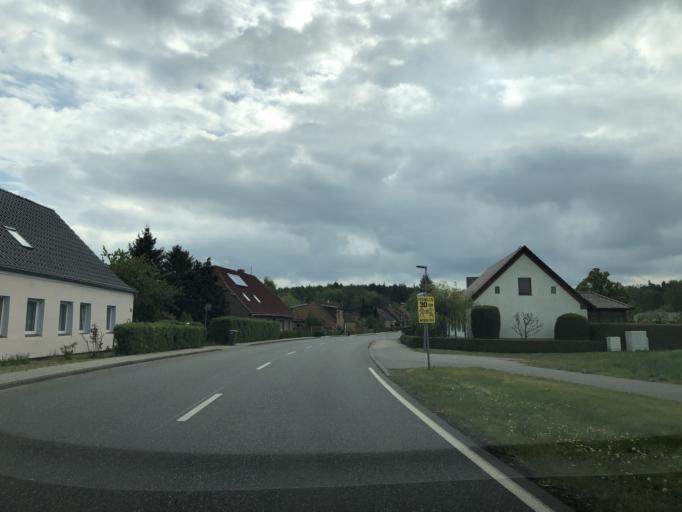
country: DE
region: Mecklenburg-Vorpommern
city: Plau am See
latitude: 53.4668
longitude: 12.1897
